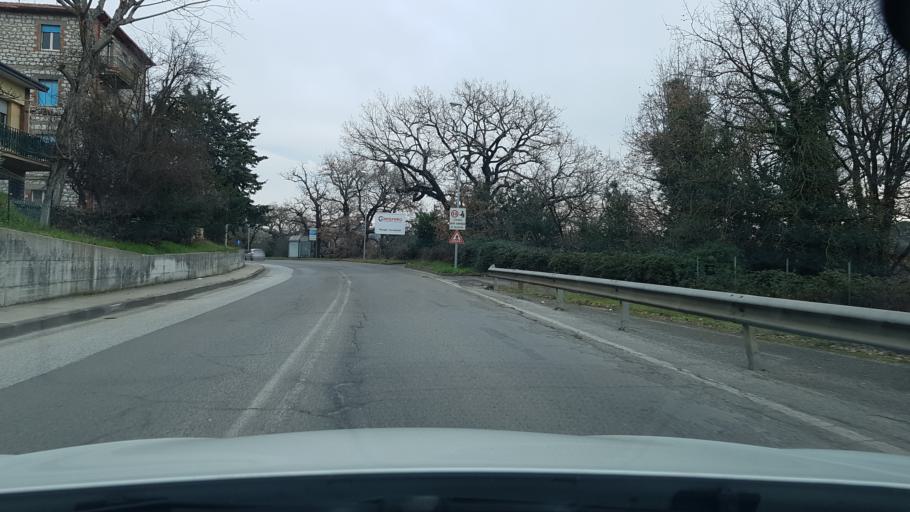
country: IT
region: Umbria
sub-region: Provincia di Perugia
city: Lacugnano
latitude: 43.1027
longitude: 12.3473
